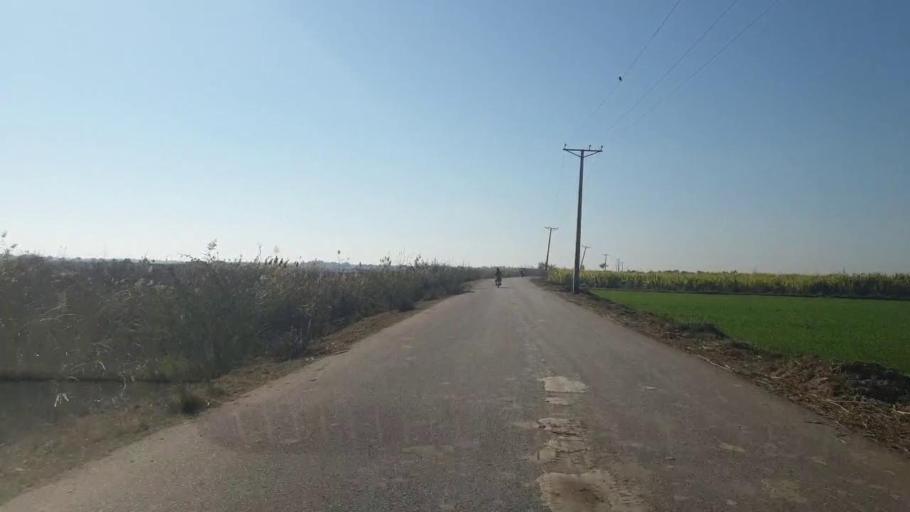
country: PK
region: Sindh
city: Kot Diji
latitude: 27.3067
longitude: 68.6461
